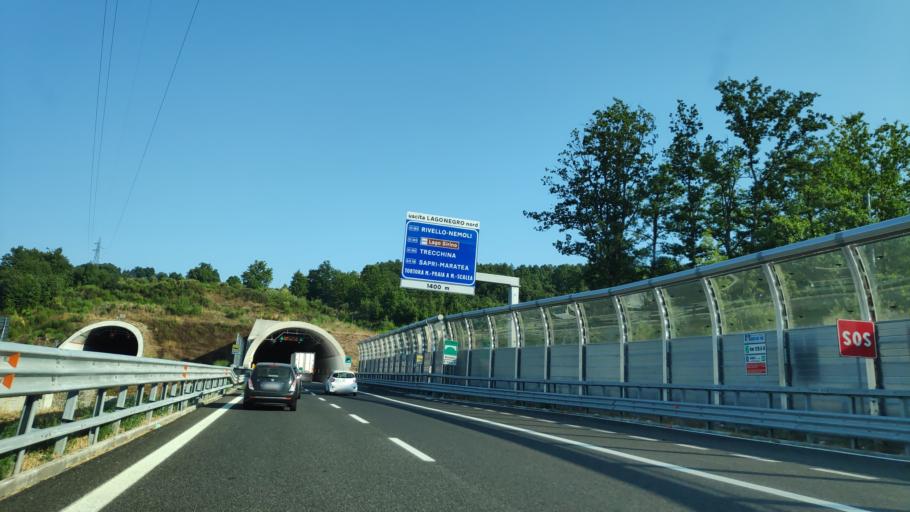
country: IT
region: Basilicate
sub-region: Provincia di Potenza
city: Lagonegro
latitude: 40.1386
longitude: 15.7587
